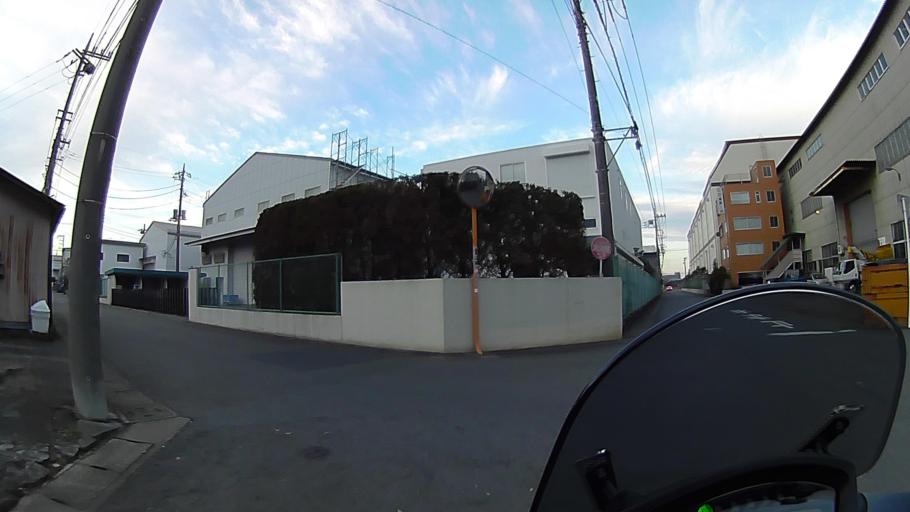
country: JP
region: Kanagawa
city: Atsugi
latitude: 35.4266
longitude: 139.4217
